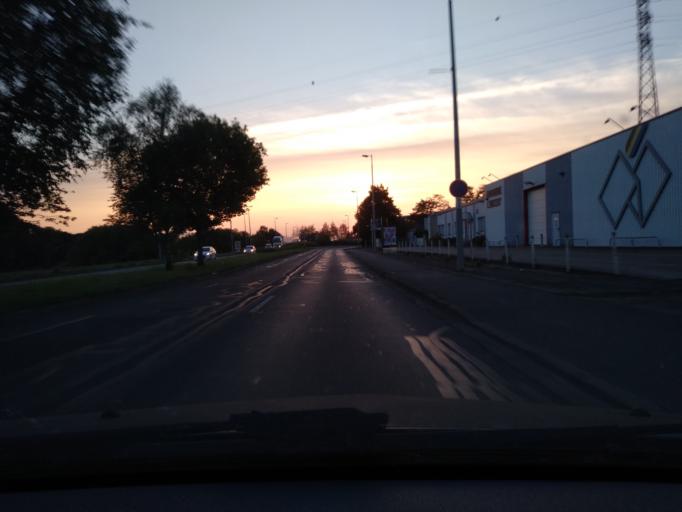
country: FR
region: Centre
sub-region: Departement d'Indre-et-Loire
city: Tours
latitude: 47.3745
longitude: 0.6731
